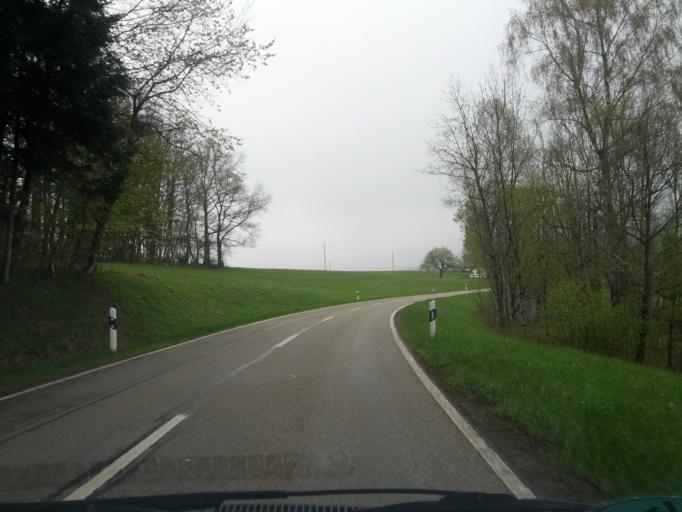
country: DE
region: Baden-Wuerttemberg
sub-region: Freiburg Region
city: Rickenbach
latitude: 47.6160
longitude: 8.0150
